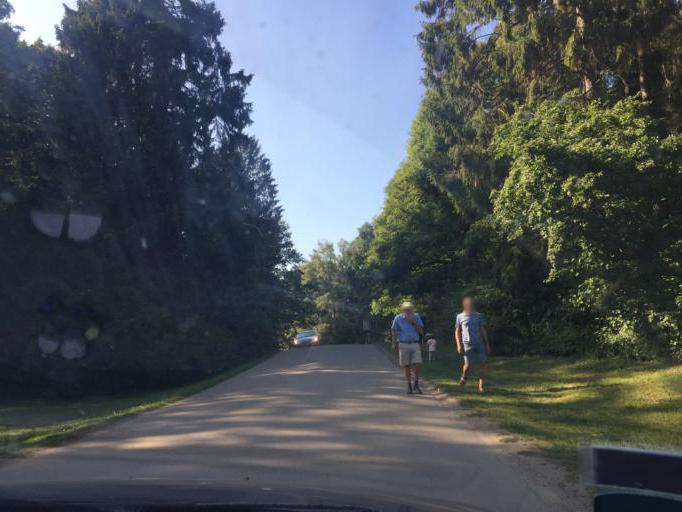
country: DK
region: Zealand
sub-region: Lolland Kommune
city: Maribo
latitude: 54.8242
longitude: 11.5083
